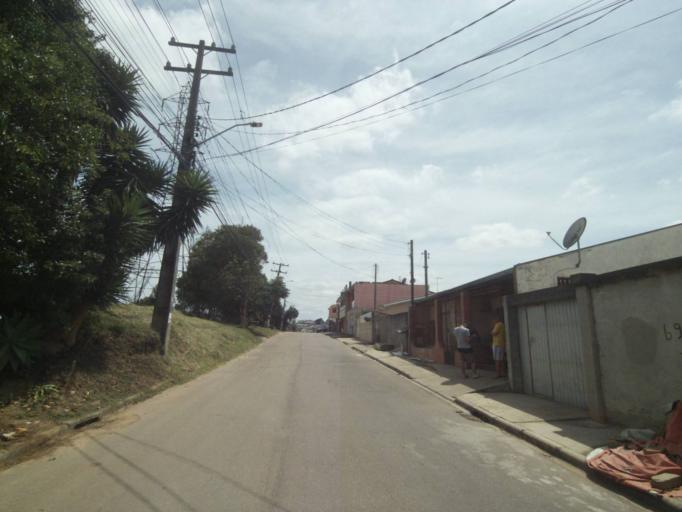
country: BR
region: Parana
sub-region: Curitiba
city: Curitiba
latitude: -25.4931
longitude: -49.3410
